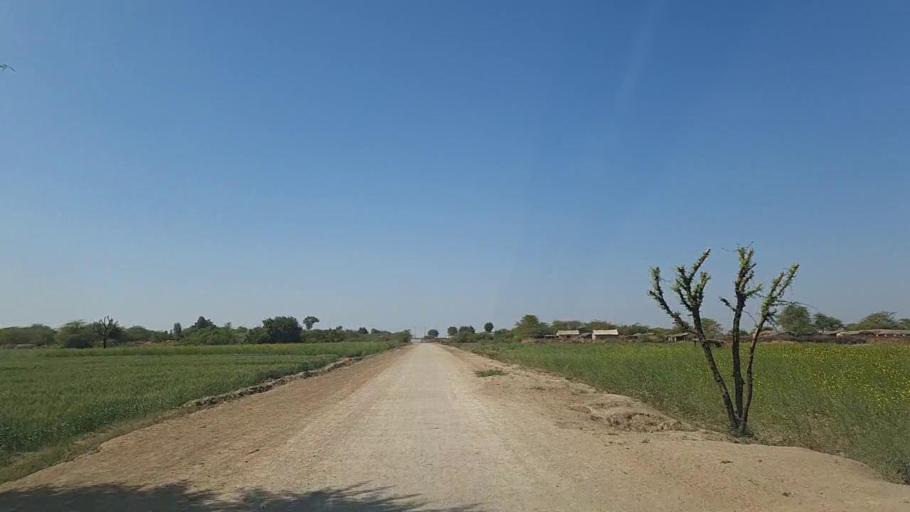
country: PK
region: Sindh
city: Samaro
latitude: 25.1026
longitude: 69.3902
